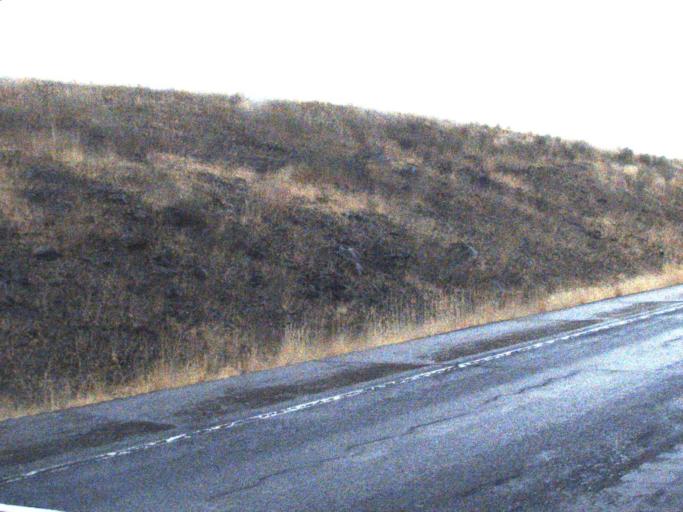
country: US
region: Washington
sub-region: Spokane County
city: Cheney
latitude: 47.2339
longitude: -117.3594
